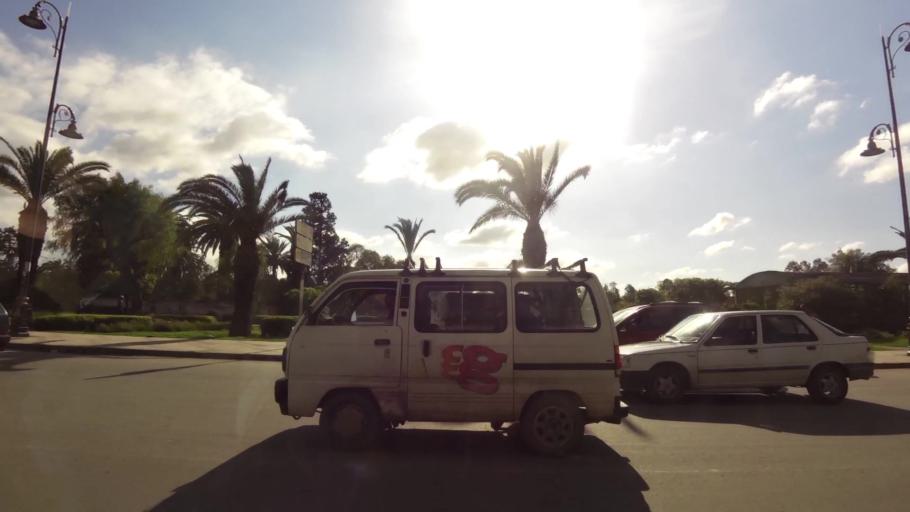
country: MA
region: Chaouia-Ouardigha
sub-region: Settat Province
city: Berrechid
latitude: 33.2623
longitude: -7.5819
